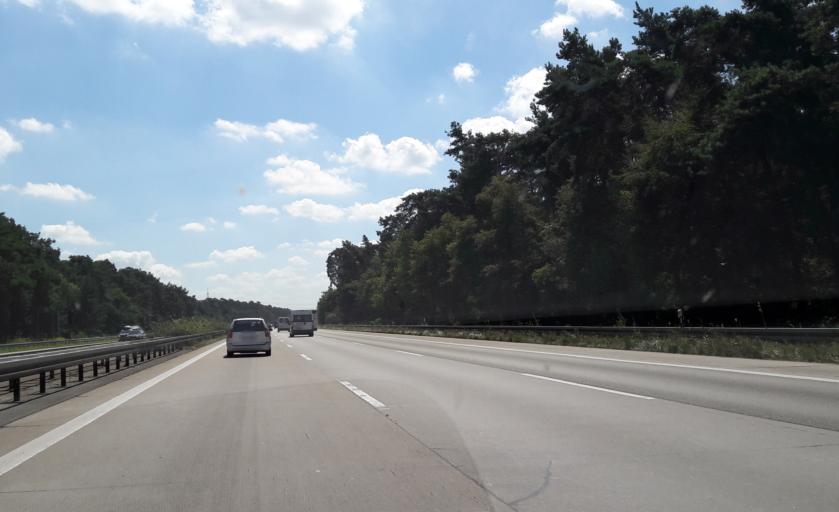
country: DE
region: Baden-Wuerttemberg
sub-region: Karlsruhe Region
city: Reilingen
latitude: 49.3119
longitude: 8.5806
